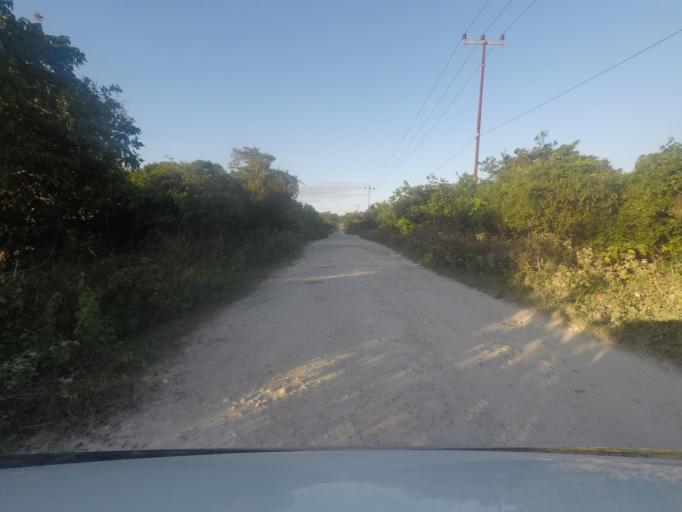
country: TL
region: Lautem
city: Lospalos
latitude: -8.3989
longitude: 127.2058
